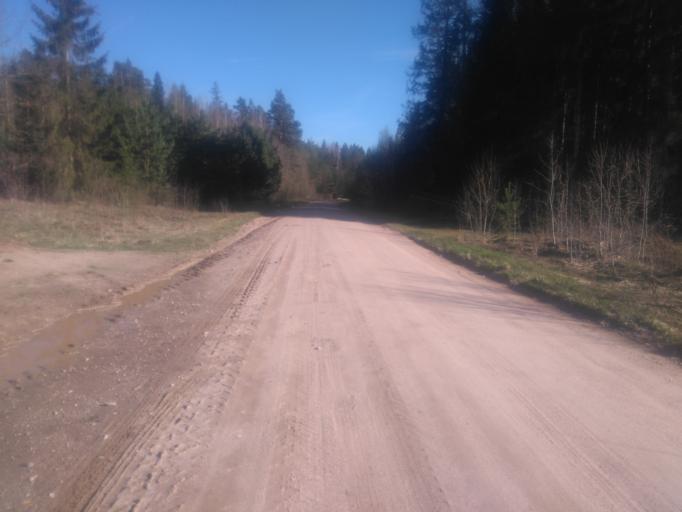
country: LV
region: Vecpiebalga
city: Vecpiebalga
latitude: 57.0127
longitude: 25.8386
